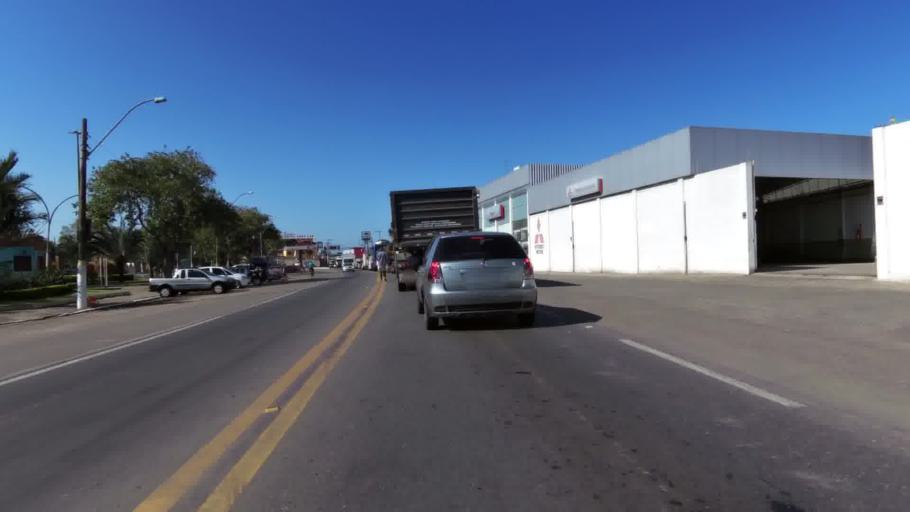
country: BR
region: Rio de Janeiro
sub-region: Campos Dos Goytacazes
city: Campos
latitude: -21.7517
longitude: -41.3390
